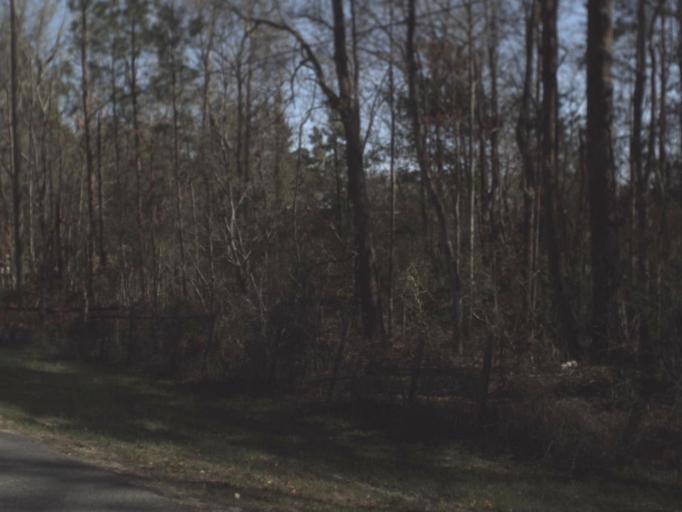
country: US
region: Florida
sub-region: Jefferson County
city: Monticello
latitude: 30.5044
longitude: -84.0242
